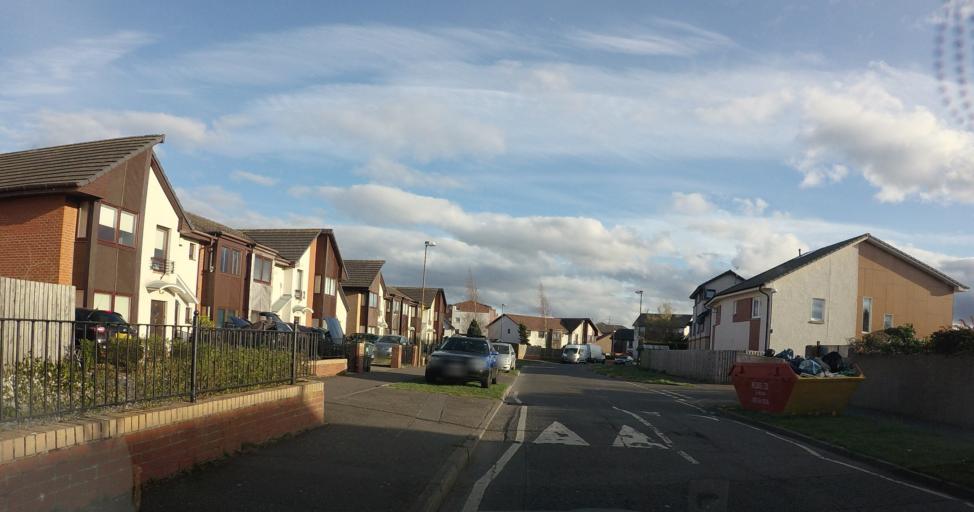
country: GB
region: Scotland
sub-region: Midlothian
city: Loanhead
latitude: 55.9008
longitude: -3.1565
